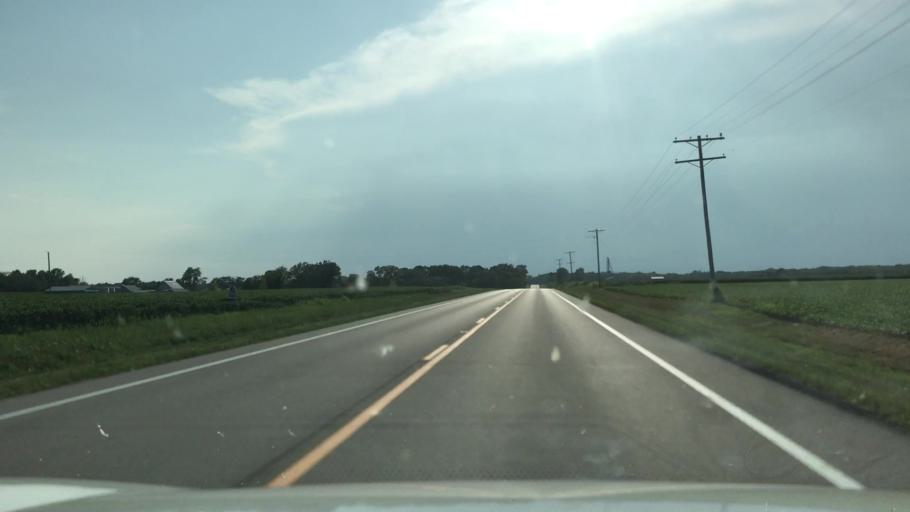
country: US
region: Illinois
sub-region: Washington County
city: Nashville
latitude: 38.4414
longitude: -89.3919
